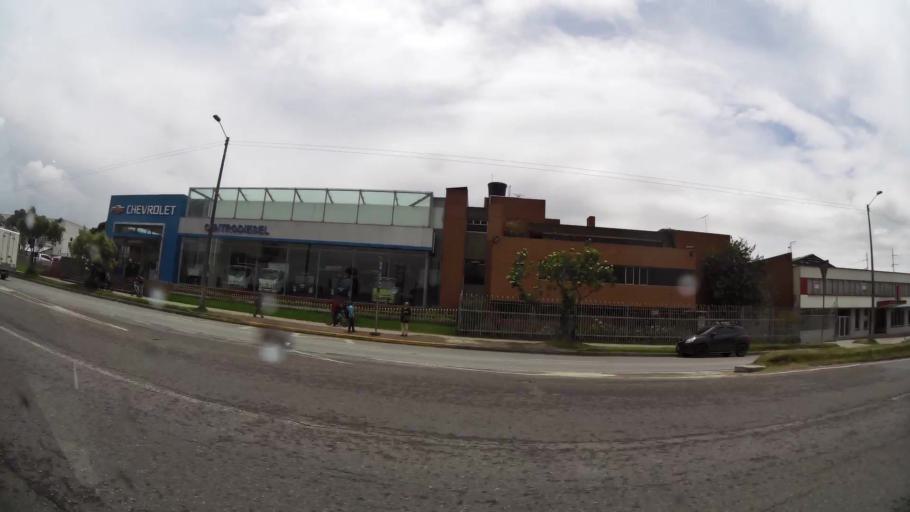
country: CO
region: Bogota D.C.
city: Bogota
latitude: 4.6389
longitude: -74.1211
